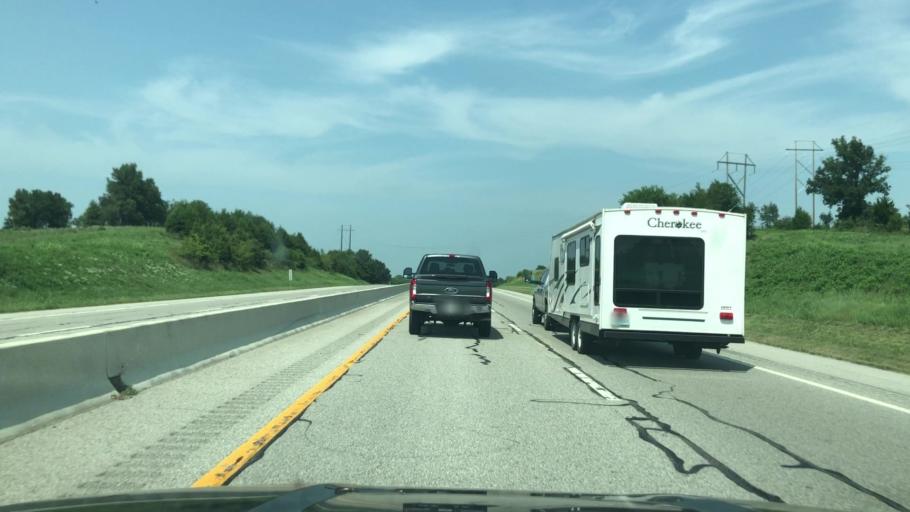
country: US
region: Oklahoma
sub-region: Ottawa County
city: Miami
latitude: 36.8325
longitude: -94.8654
